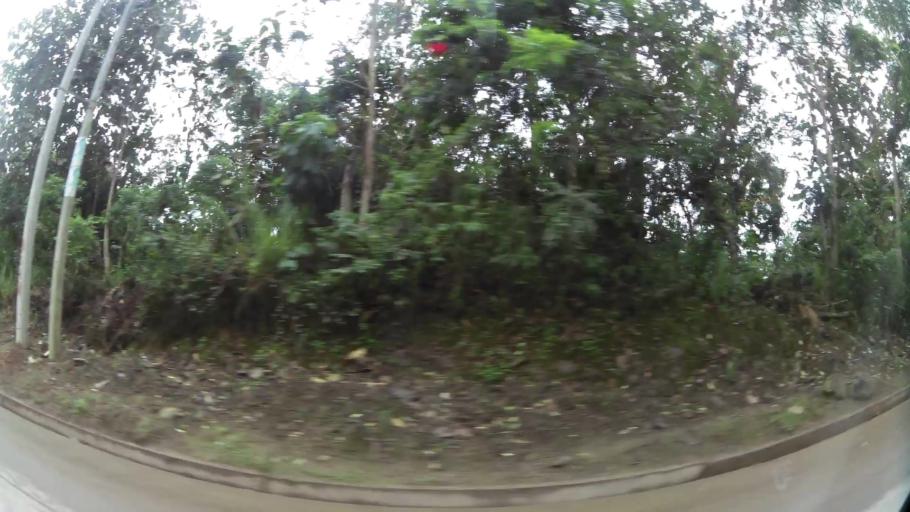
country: EC
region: El Oro
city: Pasaje
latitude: -3.3291
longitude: -79.7617
